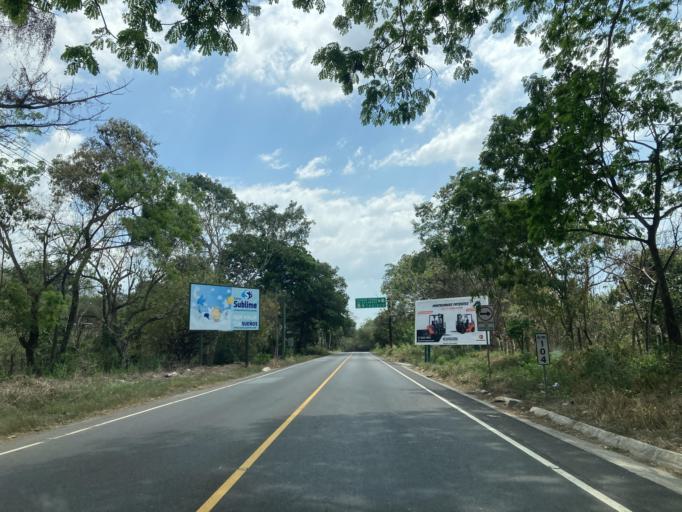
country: GT
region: Santa Rosa
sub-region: Municipio de Taxisco
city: Taxisco
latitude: 14.0774
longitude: -90.4824
